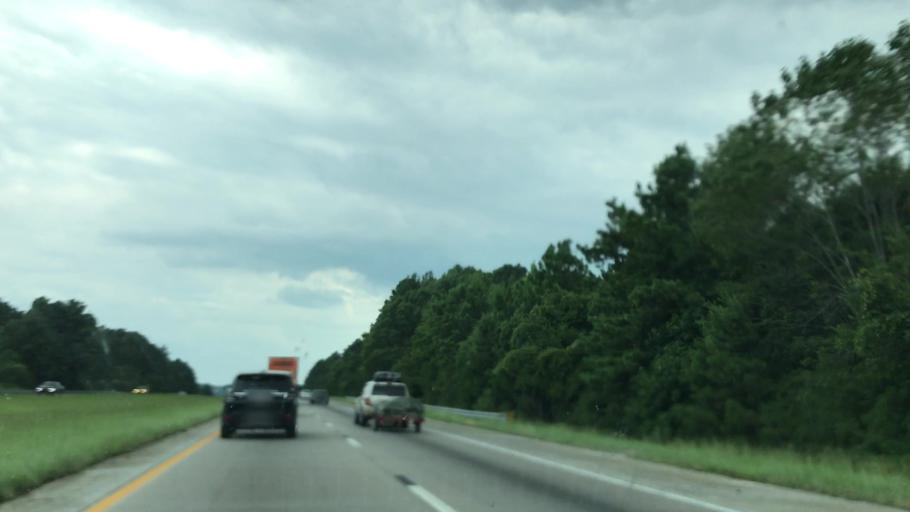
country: US
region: South Carolina
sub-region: Fairfield County
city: Winnsboro Mills
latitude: 34.3481
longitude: -81.0007
